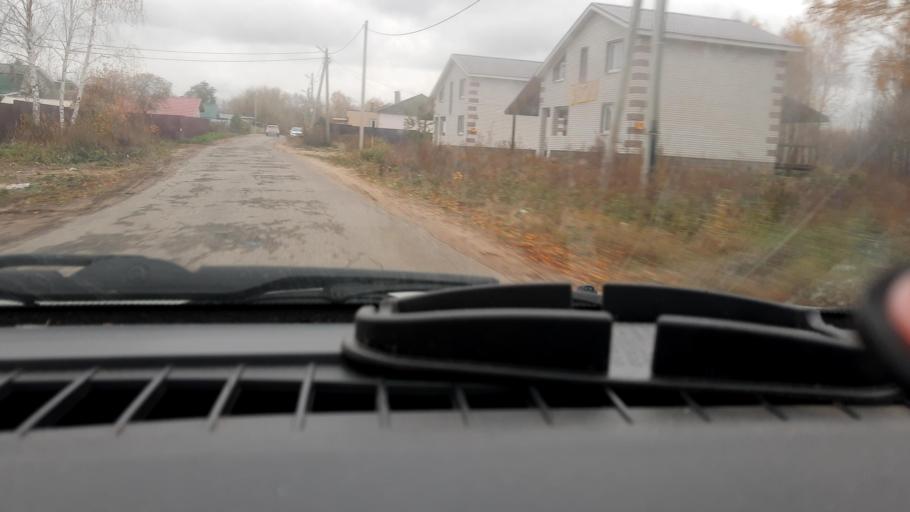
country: RU
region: Nizjnij Novgorod
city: Sitniki
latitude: 56.4157
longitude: 44.0394
